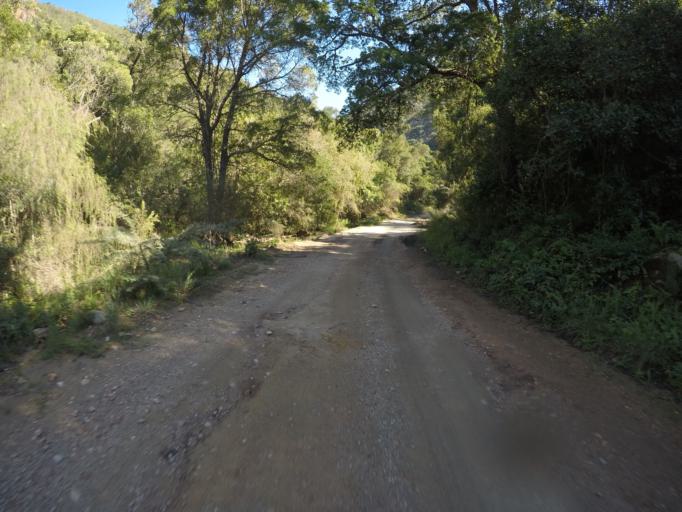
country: ZA
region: Eastern Cape
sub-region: Cacadu District Municipality
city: Kareedouw
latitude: -33.6543
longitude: 24.5228
